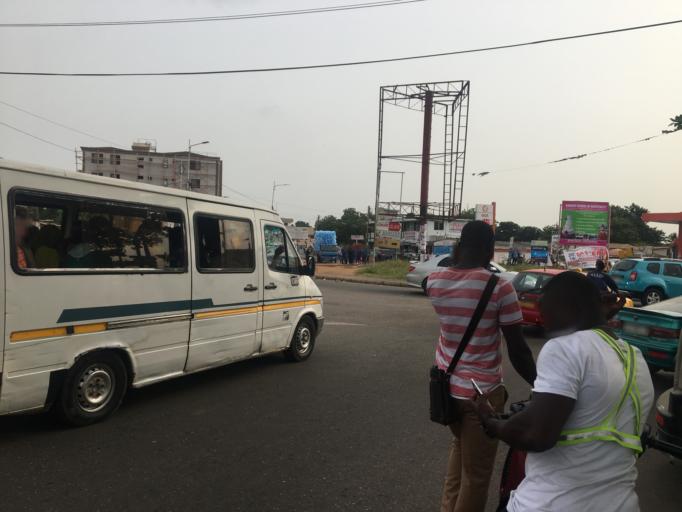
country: GH
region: Greater Accra
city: Accra
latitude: 5.5782
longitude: -0.2006
